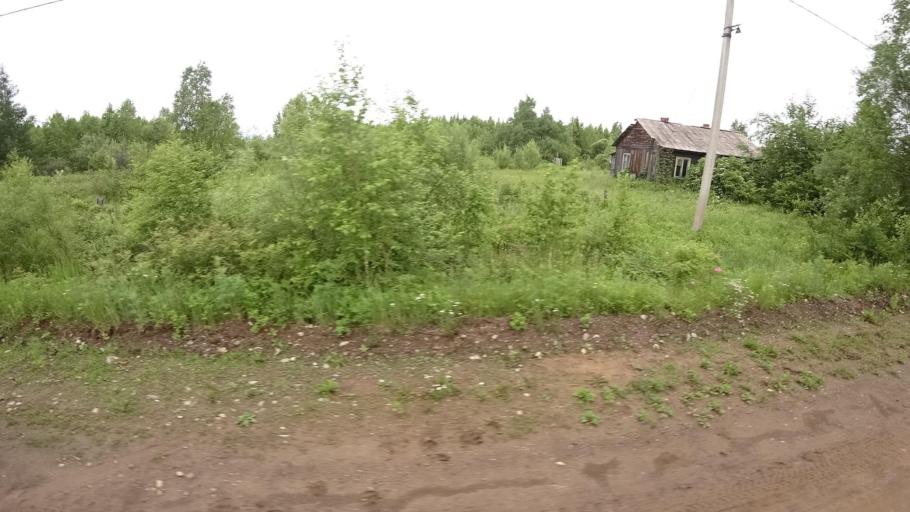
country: RU
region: Khabarovsk Krai
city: Amursk
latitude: 49.9160
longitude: 136.1622
